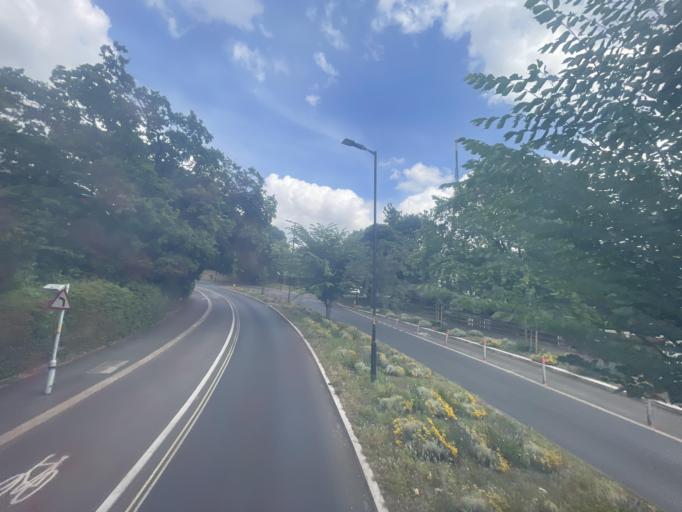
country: GB
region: England
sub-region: Greater London
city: Thornton Heath
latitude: 51.4262
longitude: -0.0797
